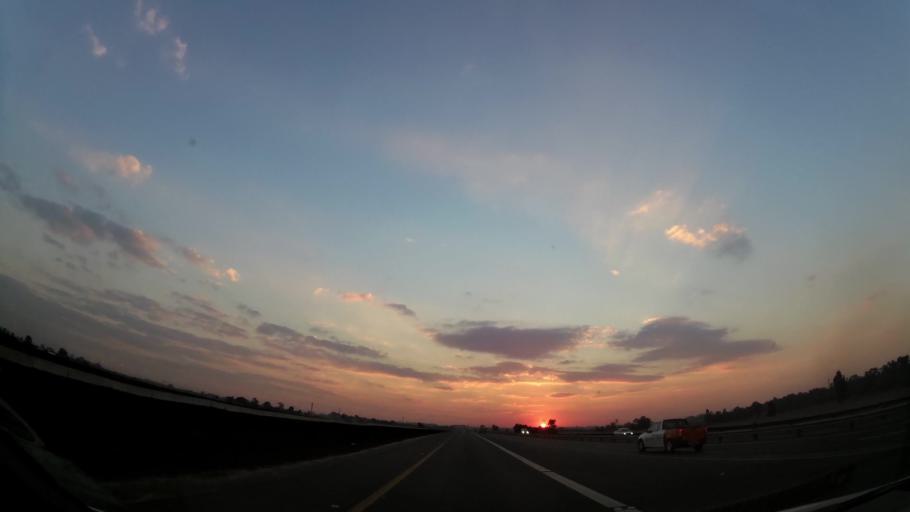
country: ZA
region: Gauteng
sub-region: Ekurhuleni Metropolitan Municipality
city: Springs
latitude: -26.2846
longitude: 28.4241
